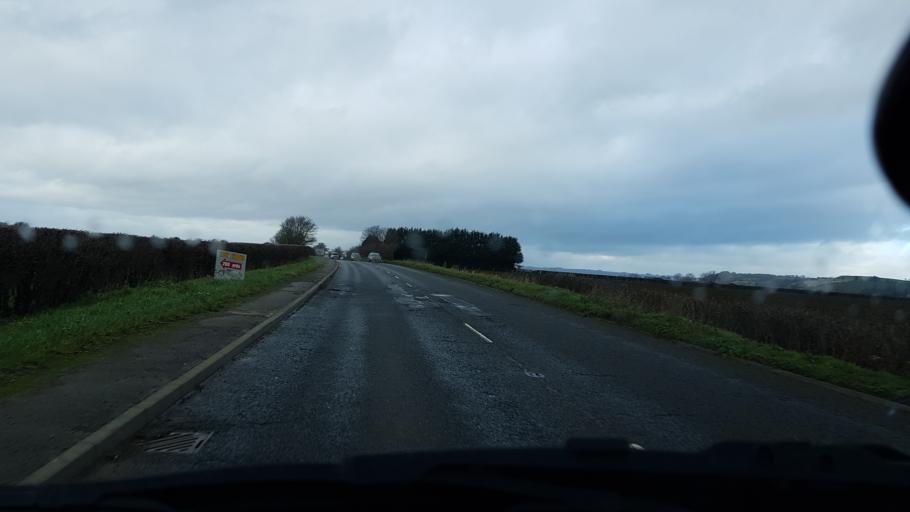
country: GB
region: England
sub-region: Gloucestershire
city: Gotherington
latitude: 51.9578
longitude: -2.0671
